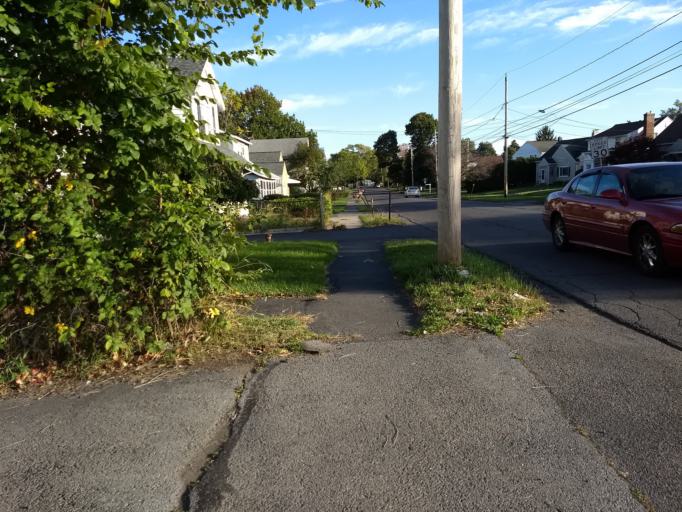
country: US
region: New York
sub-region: Onondaga County
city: Mattydale
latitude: 43.0791
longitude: -76.1521
